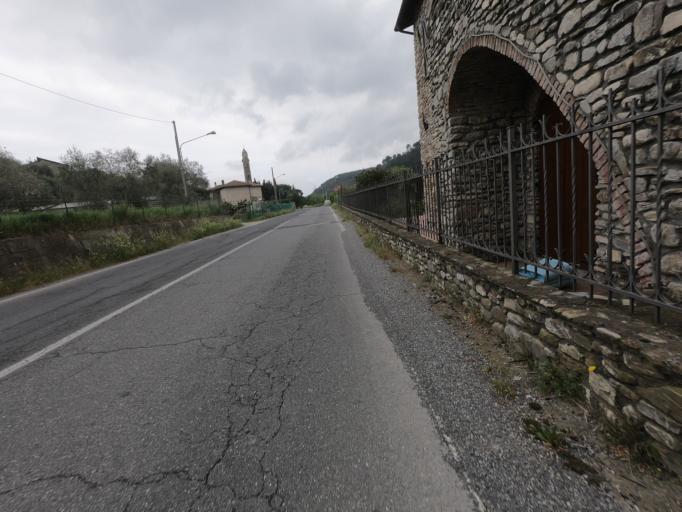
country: IT
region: Liguria
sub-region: Provincia di Savona
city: Villafranca
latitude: 43.9972
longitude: 8.1124
